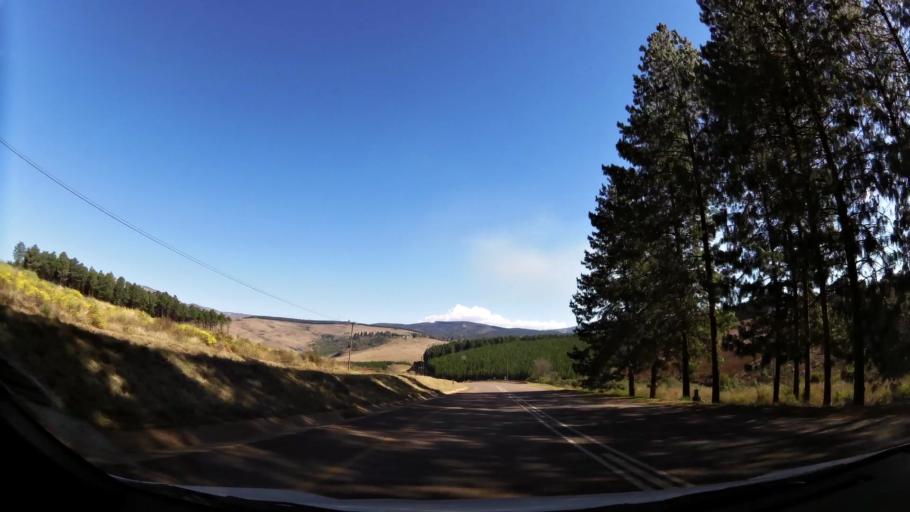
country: ZA
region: Limpopo
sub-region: Capricorn District Municipality
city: Mankoeng
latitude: -23.9346
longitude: 29.9546
